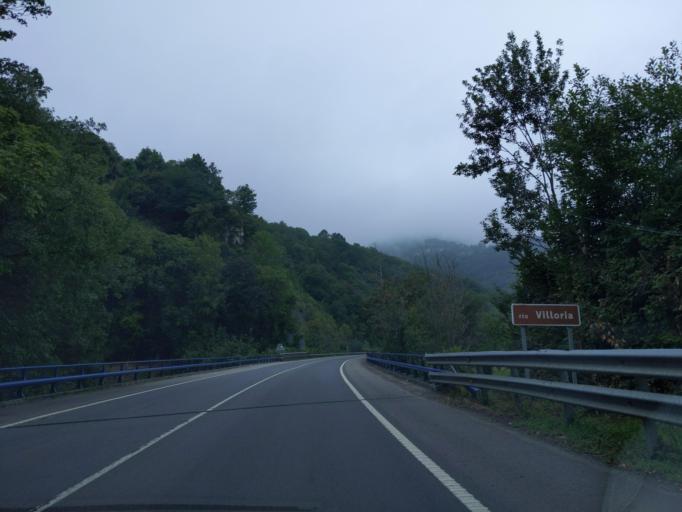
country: ES
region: Asturias
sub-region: Province of Asturias
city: Pola de Laviana
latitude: 43.2356
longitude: -5.5582
